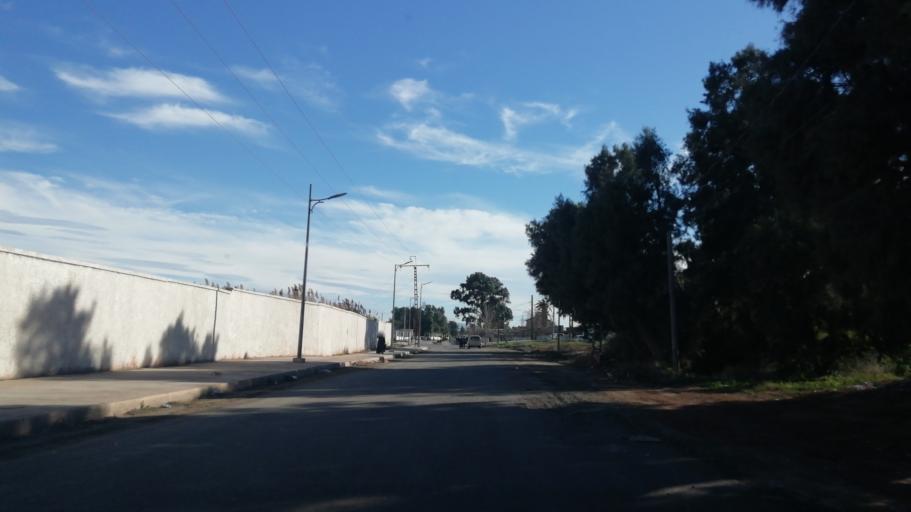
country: DZ
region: Oran
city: Es Senia
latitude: 35.6182
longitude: -0.5858
